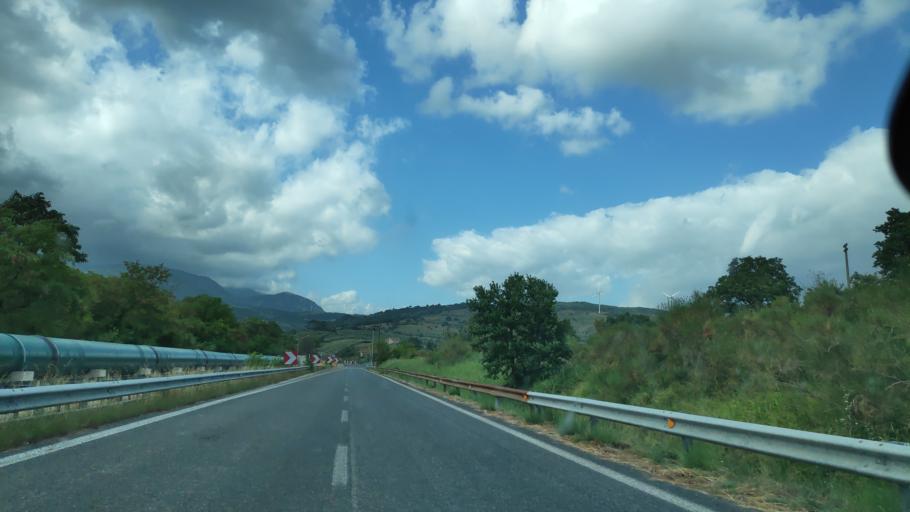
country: IT
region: Campania
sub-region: Provincia di Salerno
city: Serre
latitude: 40.6199
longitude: 15.1814
